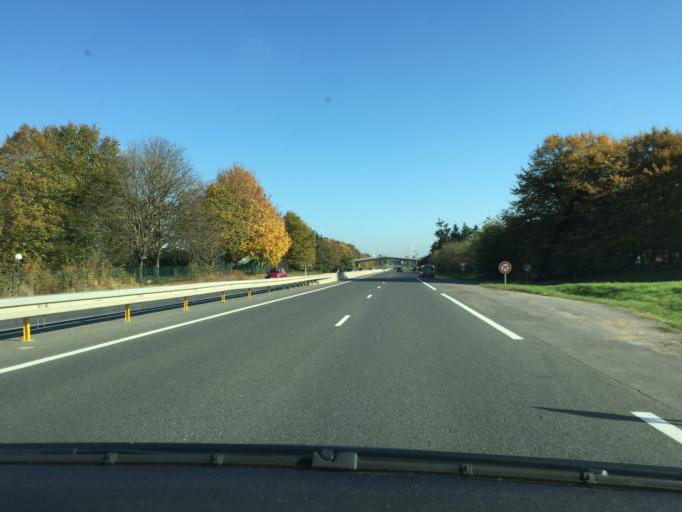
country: FR
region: Ile-de-France
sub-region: Departement de l'Essonne
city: Massy
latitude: 48.7281
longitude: 2.2916
